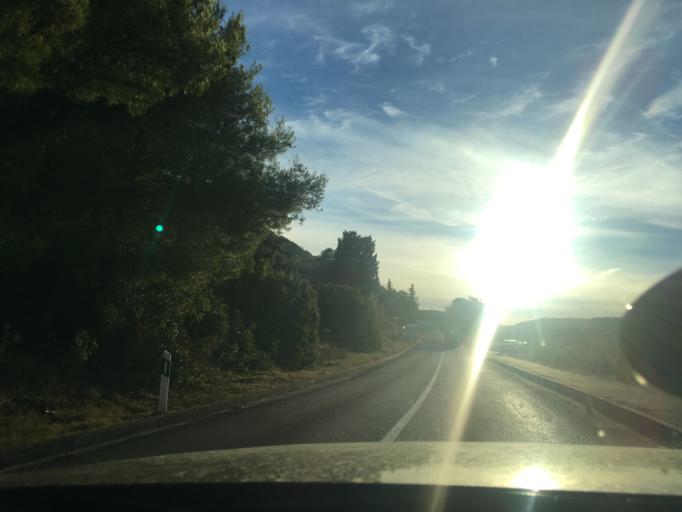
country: HR
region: Splitsko-Dalmatinska
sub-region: Grad Vis
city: Vis
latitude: 43.0575
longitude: 16.1897
